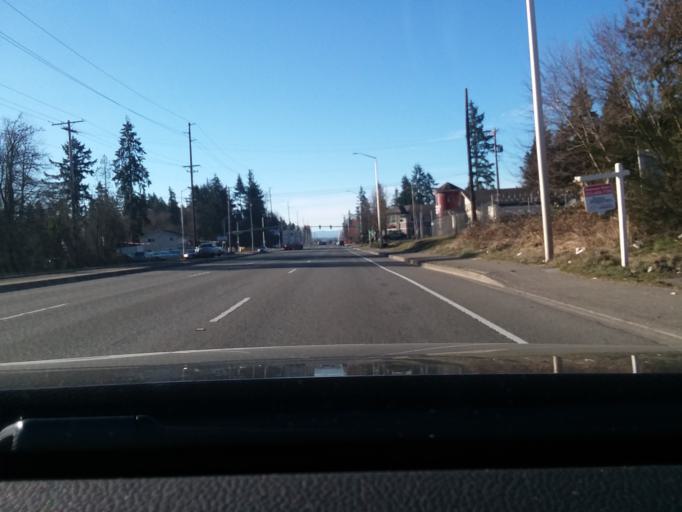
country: US
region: Washington
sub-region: Pierce County
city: Frederickson
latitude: 47.1196
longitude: -122.3577
